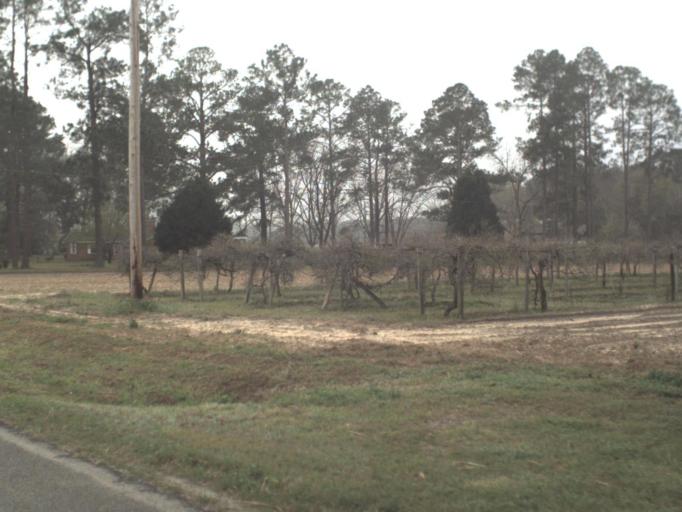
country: US
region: Florida
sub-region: Gadsden County
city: Gretna
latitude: 30.5804
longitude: -84.6728
